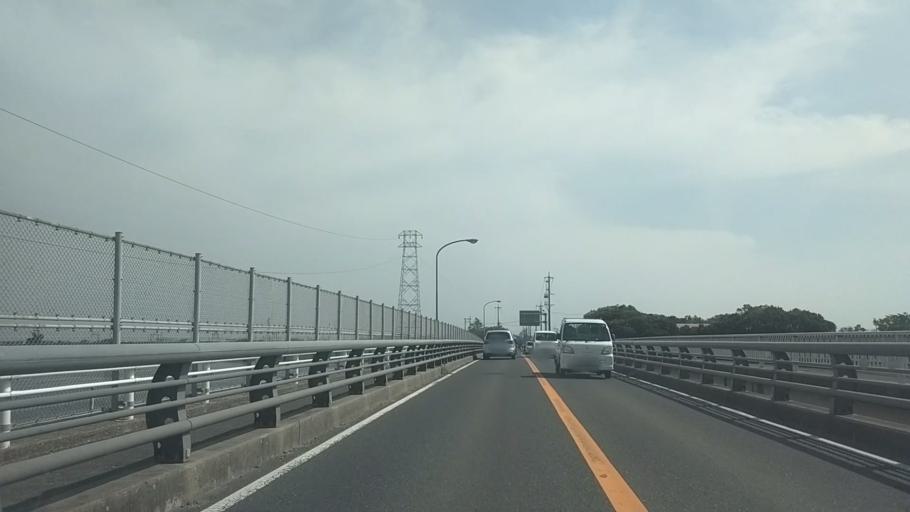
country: JP
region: Shizuoka
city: Kosai-shi
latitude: 34.6931
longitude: 137.6297
